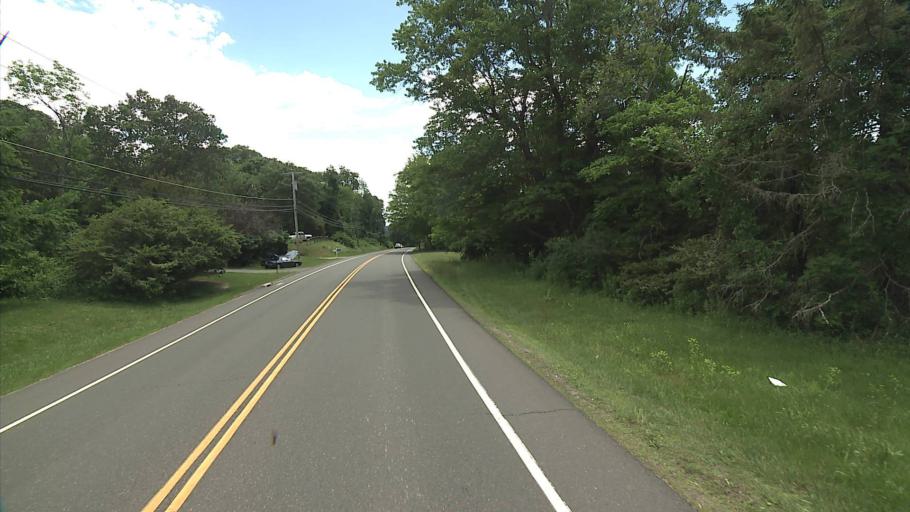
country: US
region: Connecticut
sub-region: Litchfield County
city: Watertown
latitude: 41.6285
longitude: -73.1369
